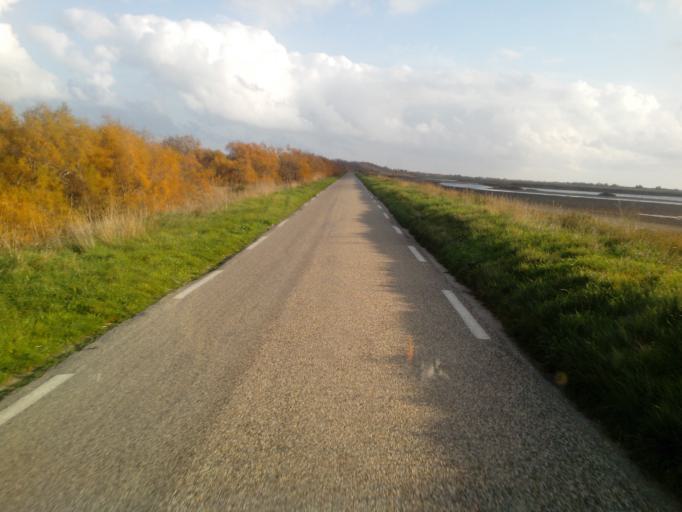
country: FR
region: Provence-Alpes-Cote d'Azur
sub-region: Departement des Bouches-du-Rhone
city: Port-Saint-Louis-du-Rhone
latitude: 43.3843
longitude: 4.7962
